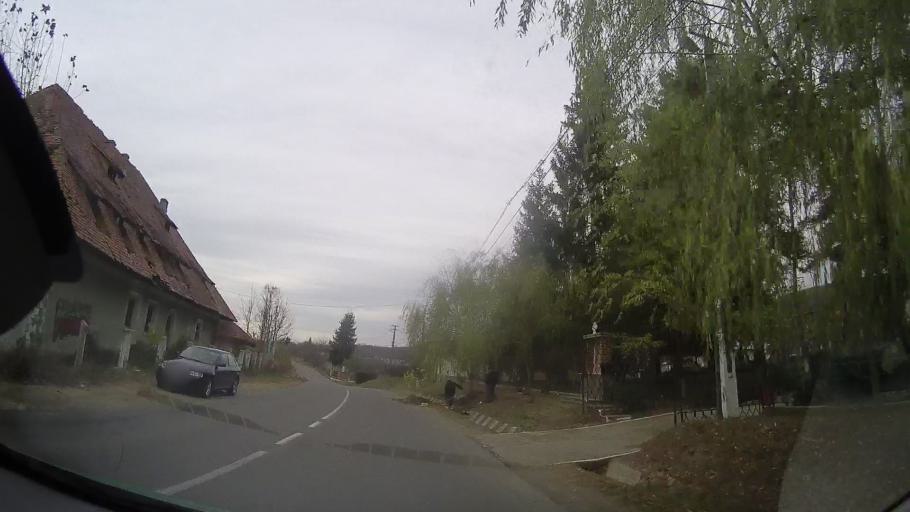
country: RO
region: Prahova
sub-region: Comuna Iordachianu
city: Iordacheanu
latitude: 45.0254
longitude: 26.2385
